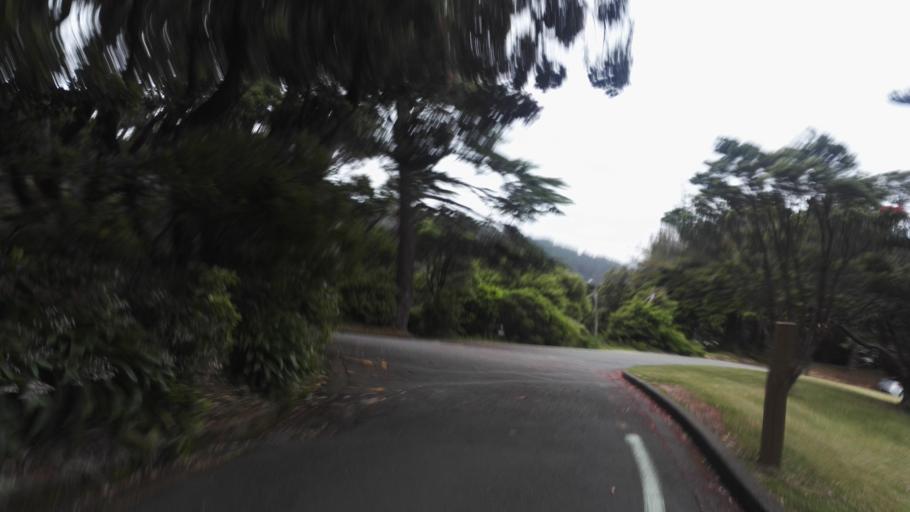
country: NZ
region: Wellington
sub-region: Wellington City
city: Kelburn
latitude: -41.2836
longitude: 174.7691
